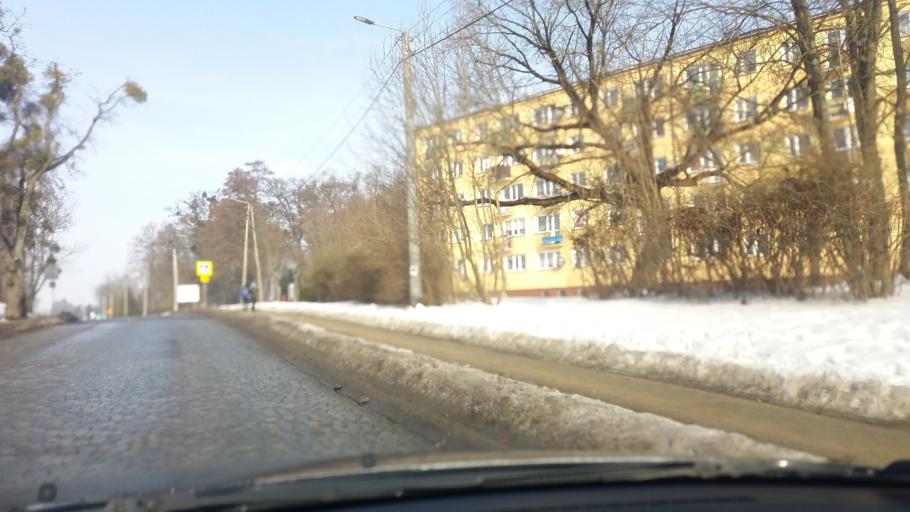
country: PL
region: Warmian-Masurian Voivodeship
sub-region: Powiat szczycienski
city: Szczytno
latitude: 53.5722
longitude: 20.9921
